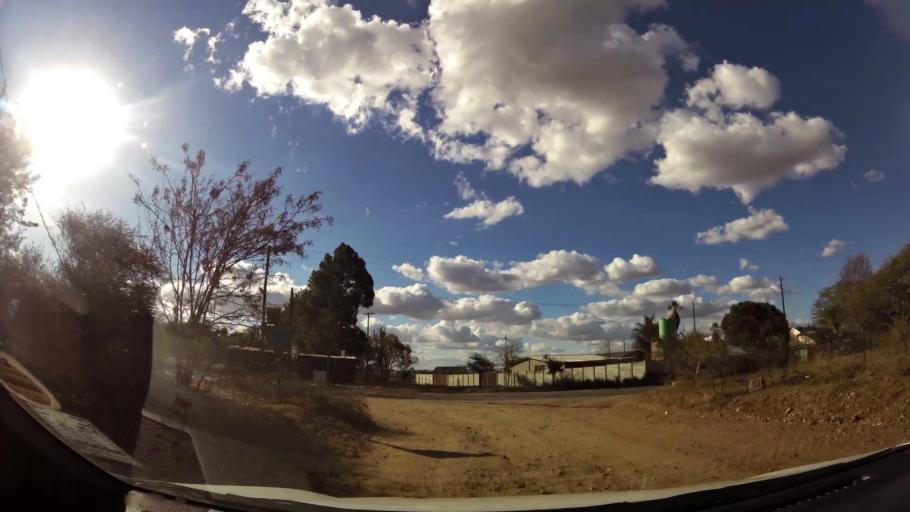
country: ZA
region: Limpopo
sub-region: Capricorn District Municipality
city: Polokwane
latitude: -23.9302
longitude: 29.4456
